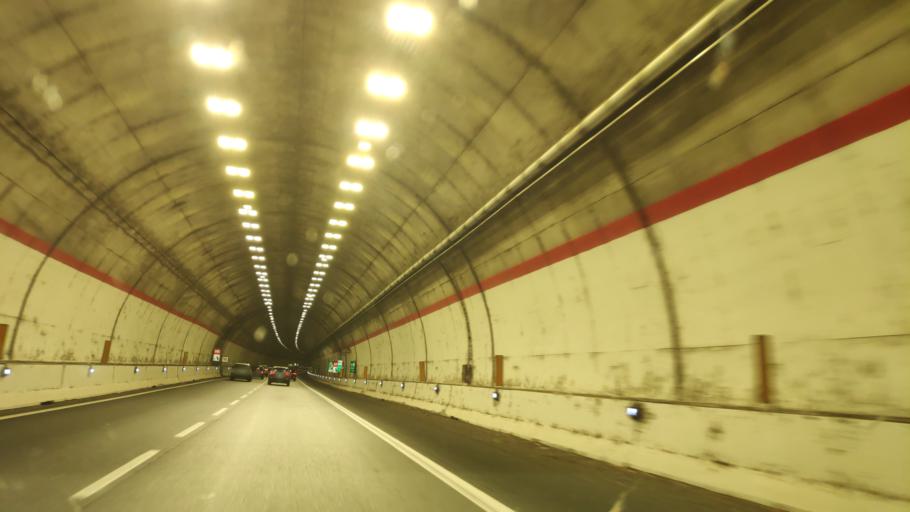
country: IT
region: Campania
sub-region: Provincia di Salerno
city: Sicignano degli Alburni
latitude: 40.6007
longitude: 15.3095
